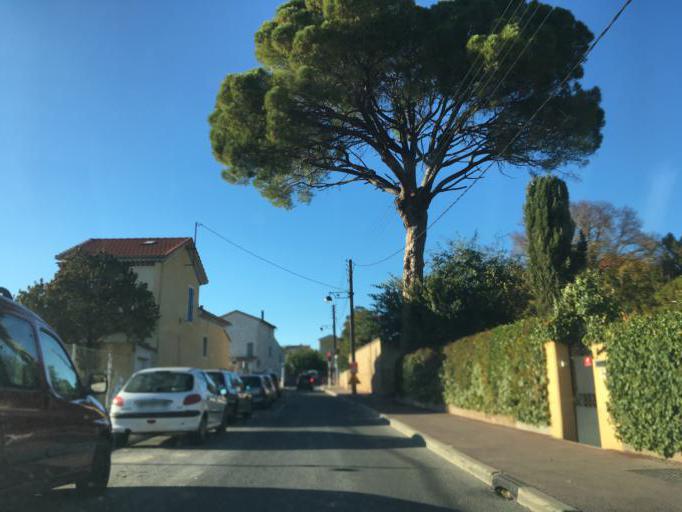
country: FR
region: Provence-Alpes-Cote d'Azur
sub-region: Departement du Var
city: Draguignan
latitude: 43.5421
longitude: 6.4603
